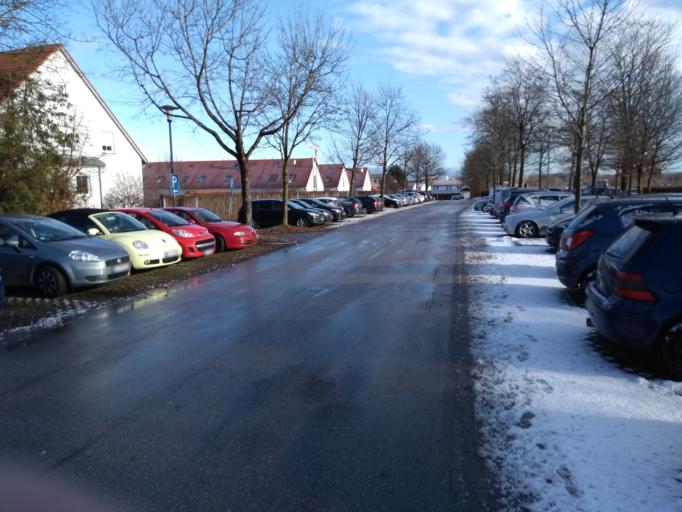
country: DE
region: Bavaria
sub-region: Upper Bavaria
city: Kaufering
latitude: 48.0817
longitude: 10.8556
